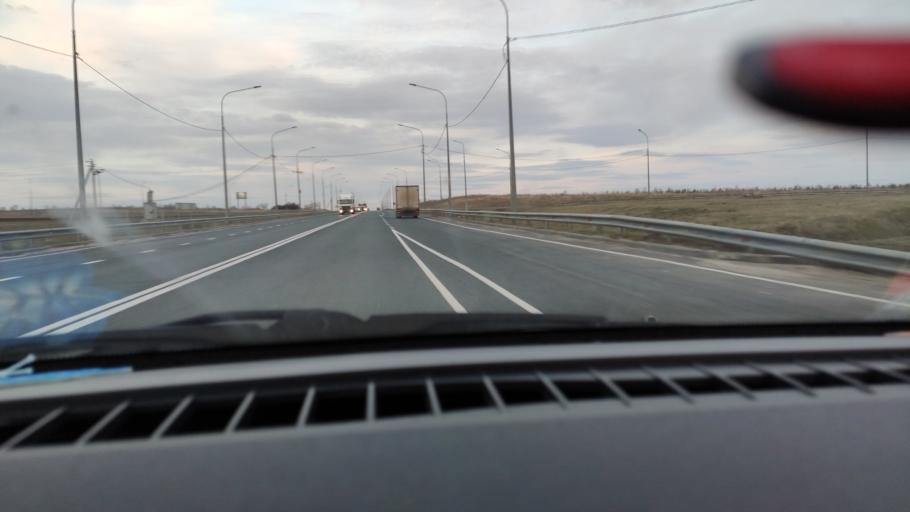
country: RU
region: Saratov
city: Yelshanka
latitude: 51.8305
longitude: 46.4301
